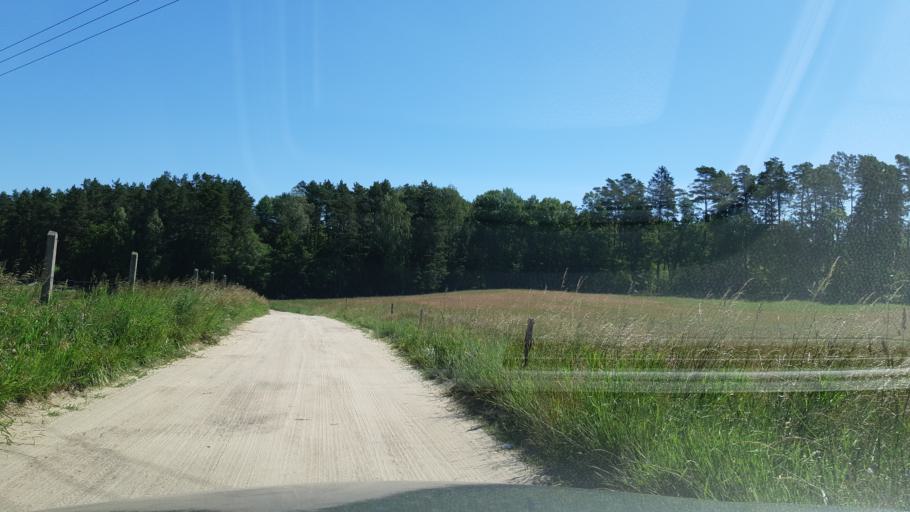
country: PL
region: Warmian-Masurian Voivodeship
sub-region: Powiat piski
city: Ruciane-Nida
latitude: 53.7095
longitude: 21.4862
